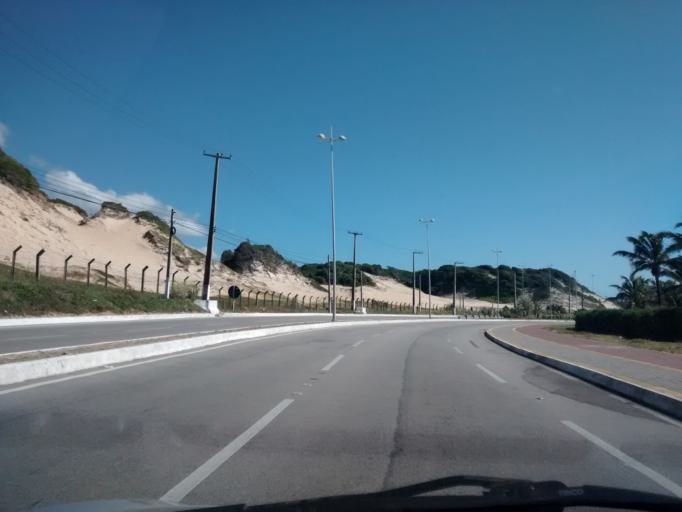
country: BR
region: Rio Grande do Norte
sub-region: Natal
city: Natal
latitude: -5.8331
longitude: -35.1829
